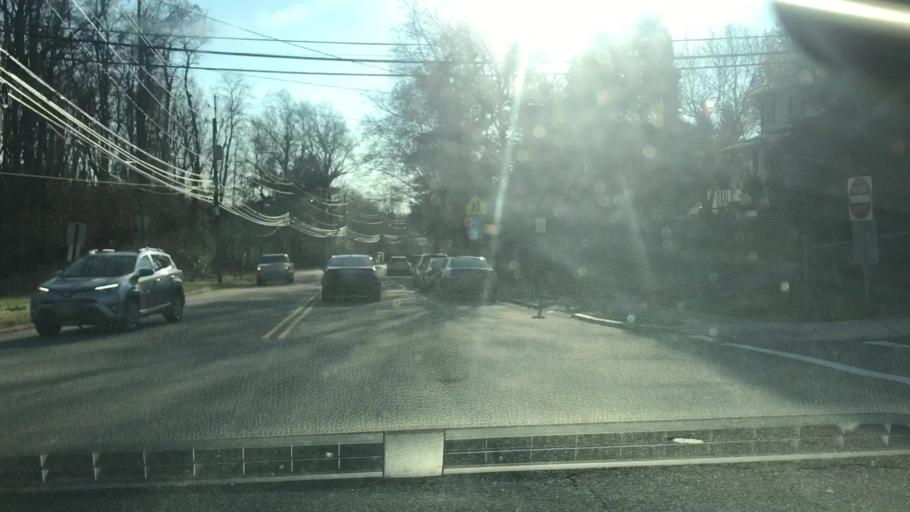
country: US
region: New Jersey
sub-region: Essex County
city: Cedar Grove
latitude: 40.8536
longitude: -74.2188
